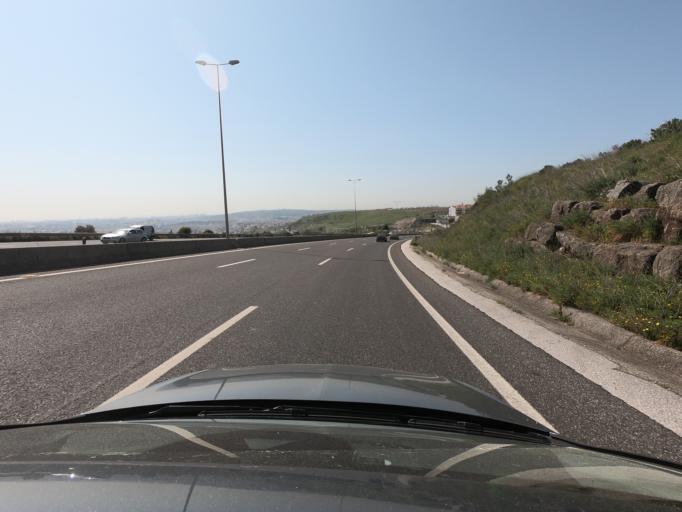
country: PT
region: Lisbon
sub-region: Odivelas
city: Famoes
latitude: 38.7830
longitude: -9.2295
